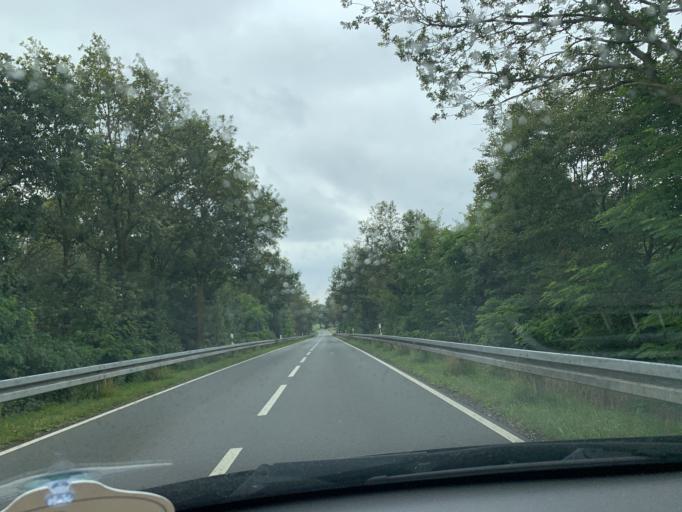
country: DE
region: North Rhine-Westphalia
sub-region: Regierungsbezirk Munster
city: Ostbevern
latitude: 52.0925
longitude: 7.8435
